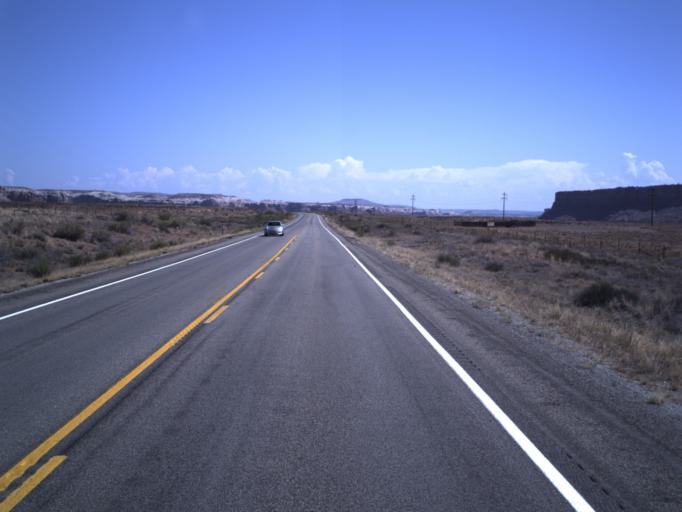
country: US
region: Utah
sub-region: San Juan County
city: Blanding
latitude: 37.2677
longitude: -109.6063
